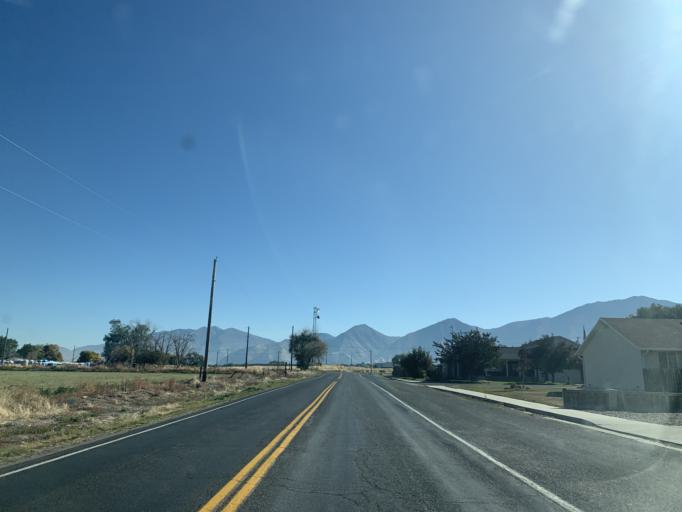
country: US
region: Utah
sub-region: Utah County
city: West Mountain
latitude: 40.0413
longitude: -111.7641
